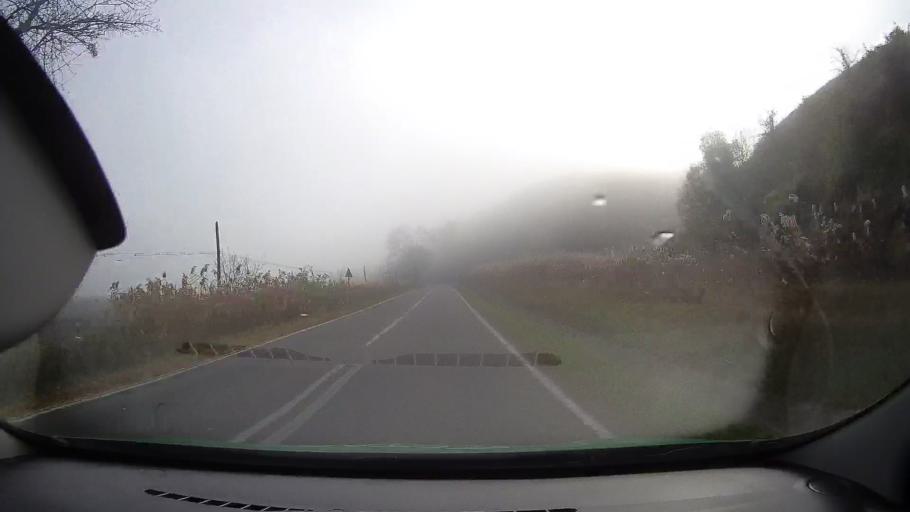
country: RO
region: Tulcea
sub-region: Comuna Nufaru
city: Malcoci
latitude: 45.1466
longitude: 28.8951
